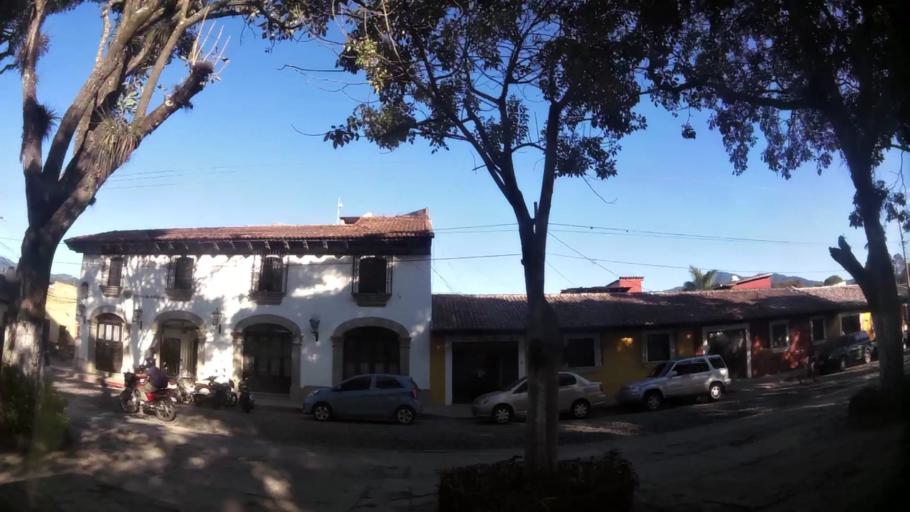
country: GT
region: Sacatepequez
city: Antigua Guatemala
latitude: 14.5550
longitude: -90.7380
